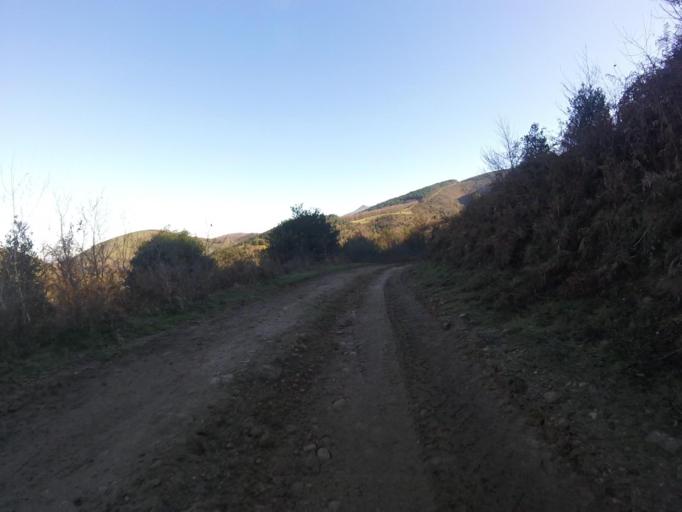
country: ES
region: Navarre
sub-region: Provincia de Navarra
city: Bera
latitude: 43.3168
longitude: -1.7149
